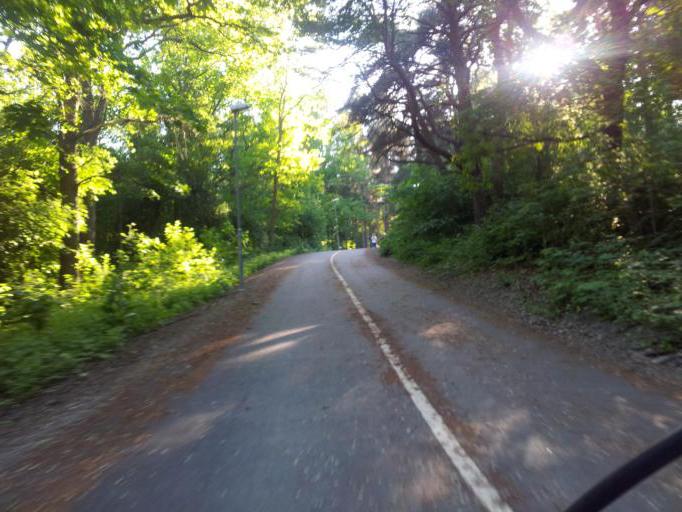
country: SE
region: Uppsala
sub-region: Uppsala Kommun
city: Gamla Uppsala
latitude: 59.8789
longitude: 17.6311
